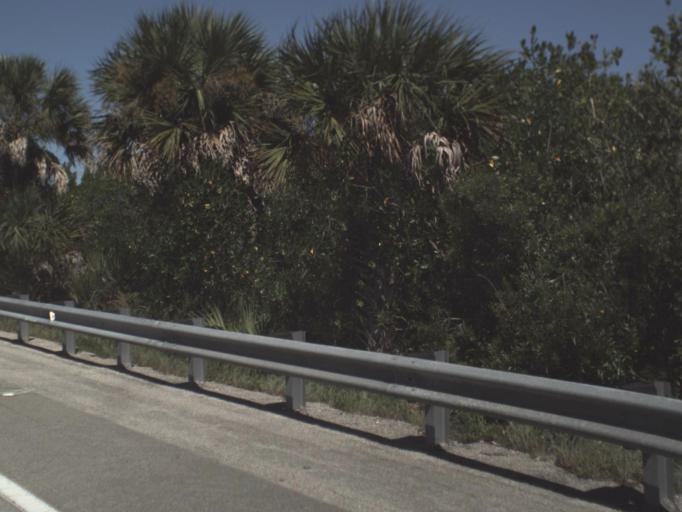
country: US
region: Florida
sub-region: Collier County
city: Marco
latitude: 25.9771
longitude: -81.5570
